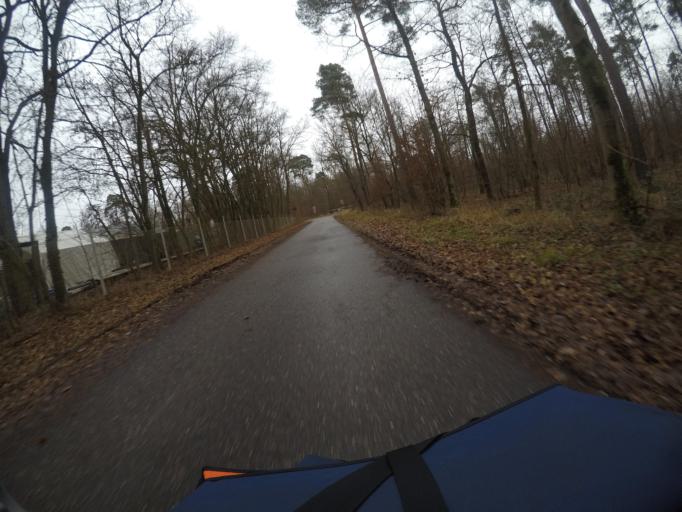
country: DE
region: Baden-Wuerttemberg
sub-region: Karlsruhe Region
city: Philippsburg
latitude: 49.2205
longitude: 8.4781
